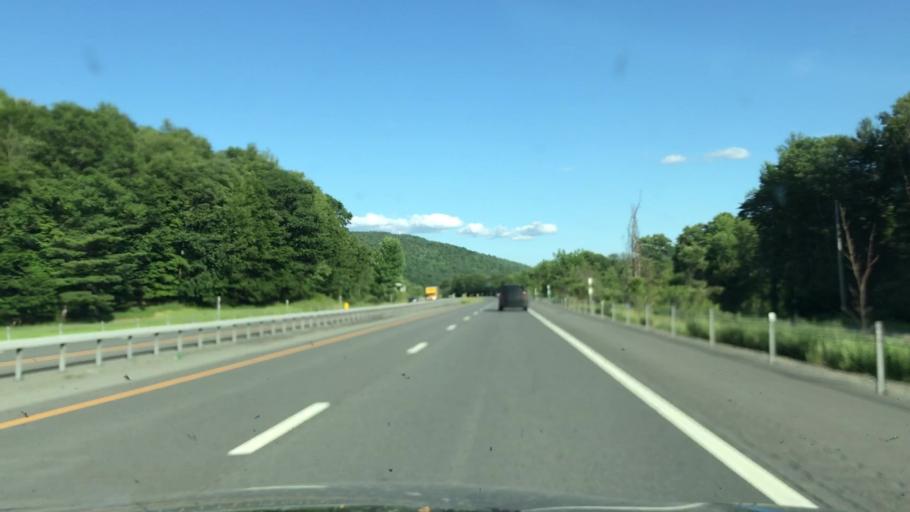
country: US
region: New York
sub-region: Delaware County
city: Hancock
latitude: 41.9840
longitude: -75.1122
